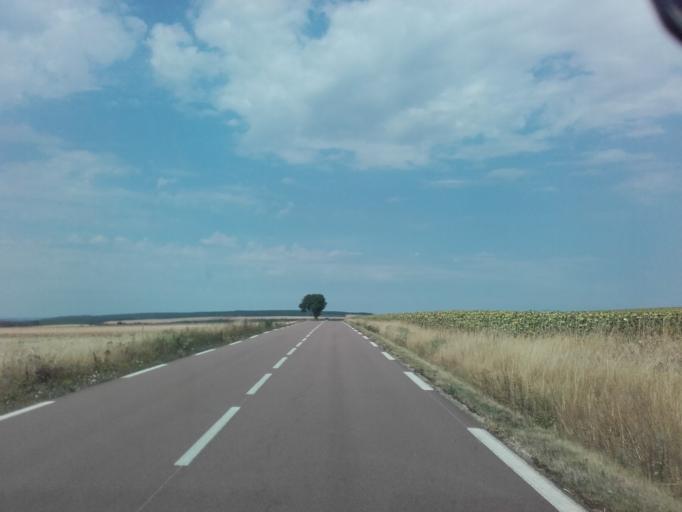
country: FR
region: Bourgogne
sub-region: Departement de l'Yonne
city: Joux-la-Ville
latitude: 47.7149
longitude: 3.8527
